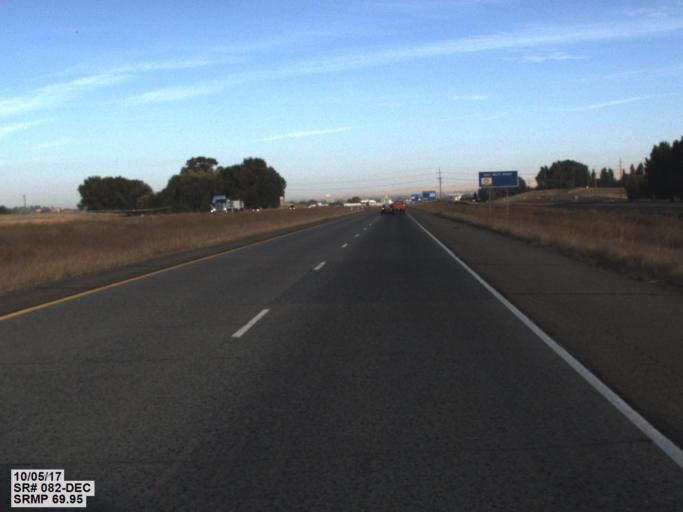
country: US
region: Washington
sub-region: Yakima County
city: Sunnyside
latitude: 46.2988
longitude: -119.9616
